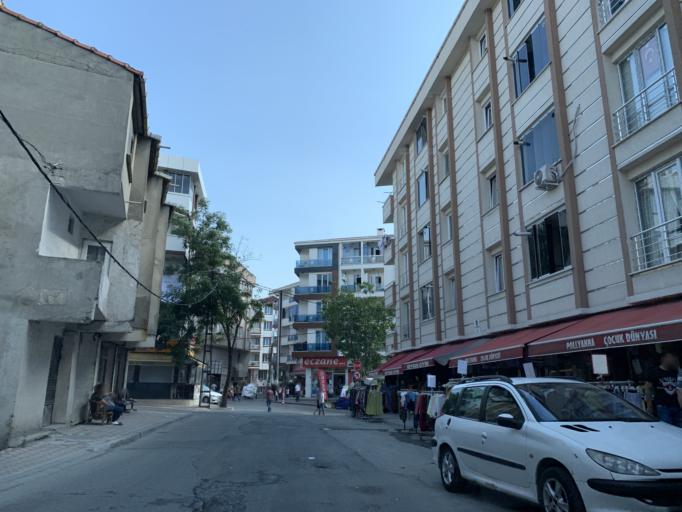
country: TR
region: Istanbul
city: Esenyurt
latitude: 41.0356
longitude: 28.6754
